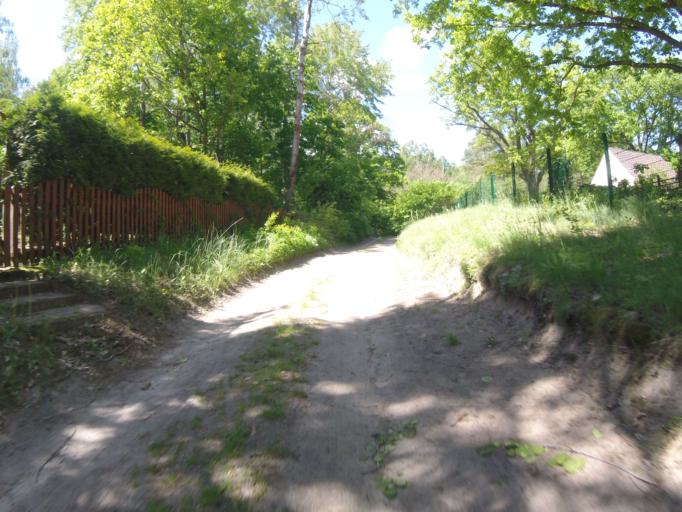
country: DE
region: Brandenburg
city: Teupitz
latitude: 52.1245
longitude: 13.5950
